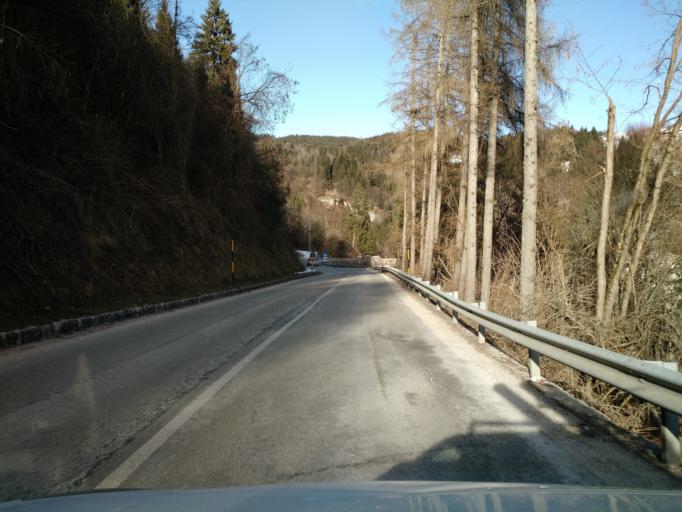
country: IT
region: Veneto
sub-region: Provincia di Vicenza
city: Canove di Roana
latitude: 45.8760
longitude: 11.4716
